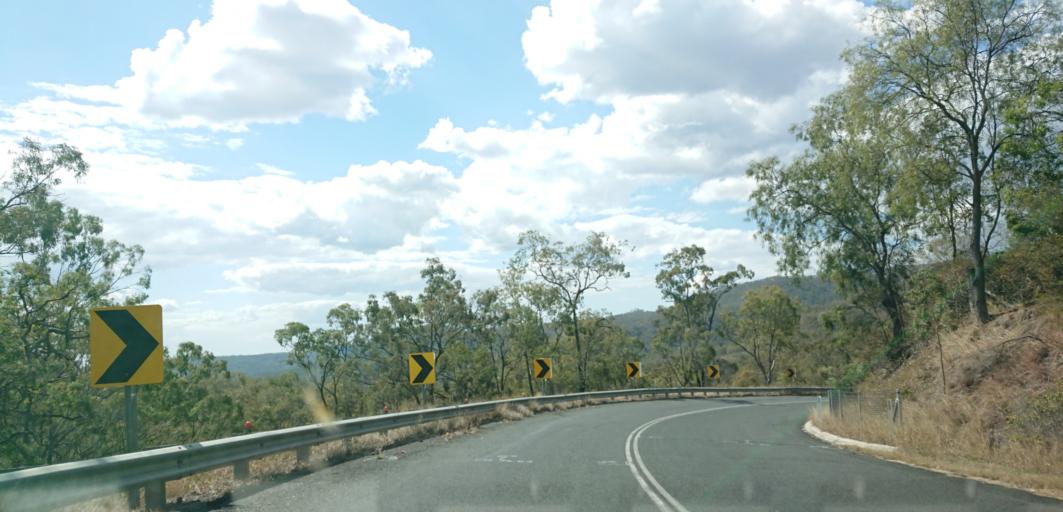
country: AU
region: Queensland
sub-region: Toowoomba
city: Top Camp
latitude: -27.8187
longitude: 152.1026
